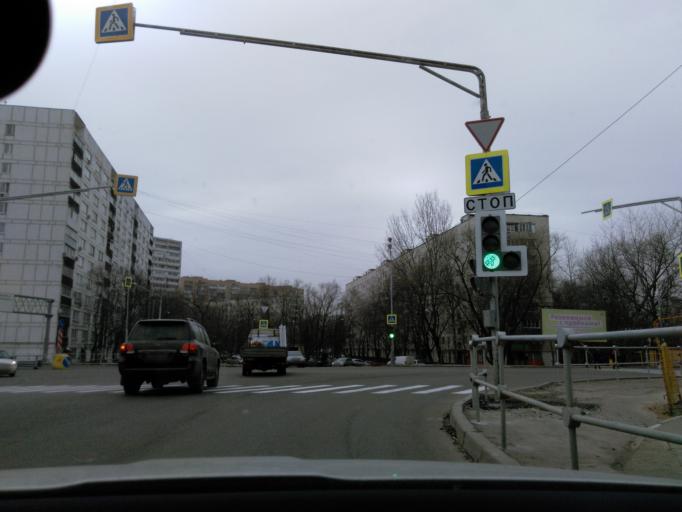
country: RU
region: Moscow
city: Novokhovrino
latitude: 55.8642
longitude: 37.5085
